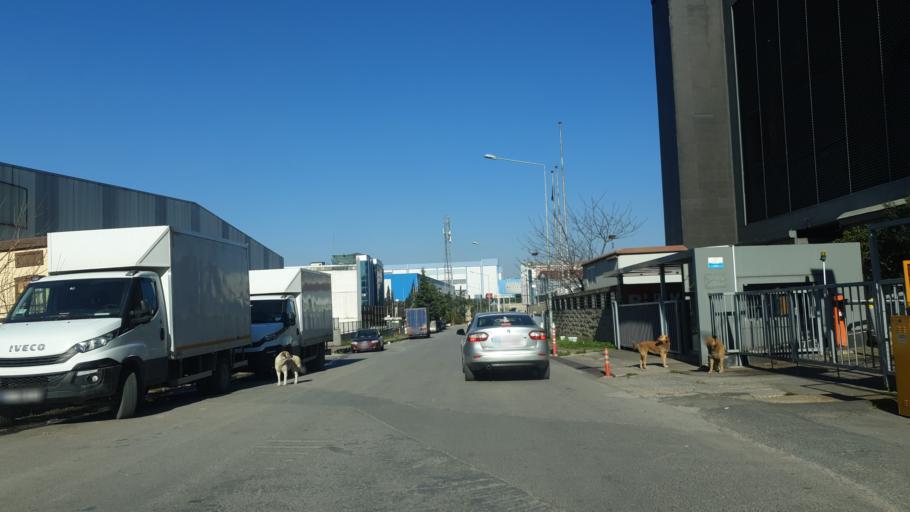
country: TR
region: Kocaeli
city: Balcik
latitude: 40.8761
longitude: 29.3738
